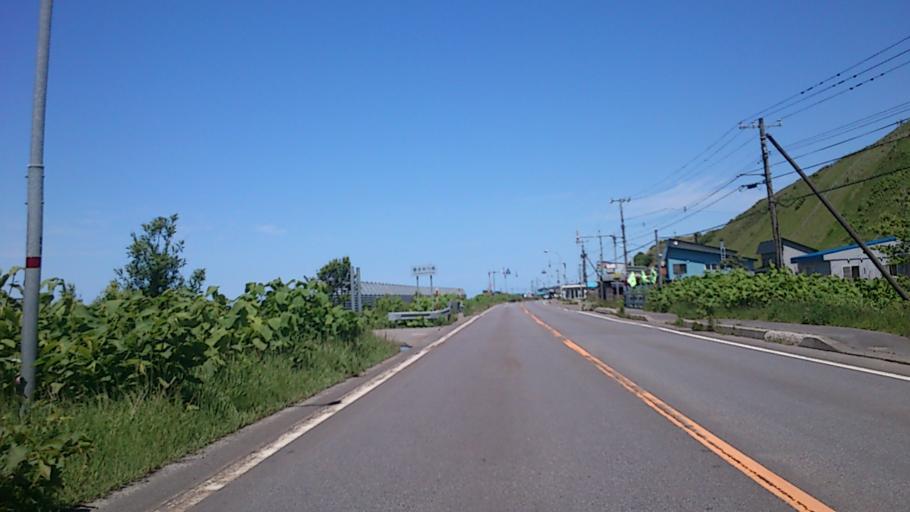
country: JP
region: Hokkaido
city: Rumoi
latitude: 43.9733
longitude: 141.6464
